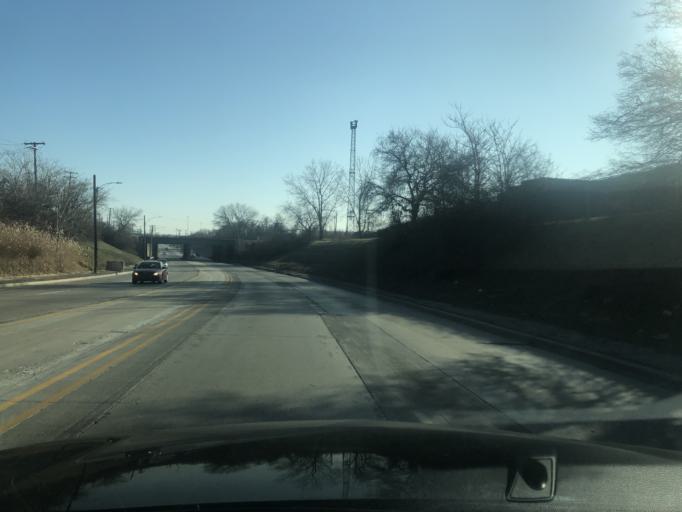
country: US
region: Michigan
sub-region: Wayne County
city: Melvindale
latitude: 42.2827
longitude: -83.1622
